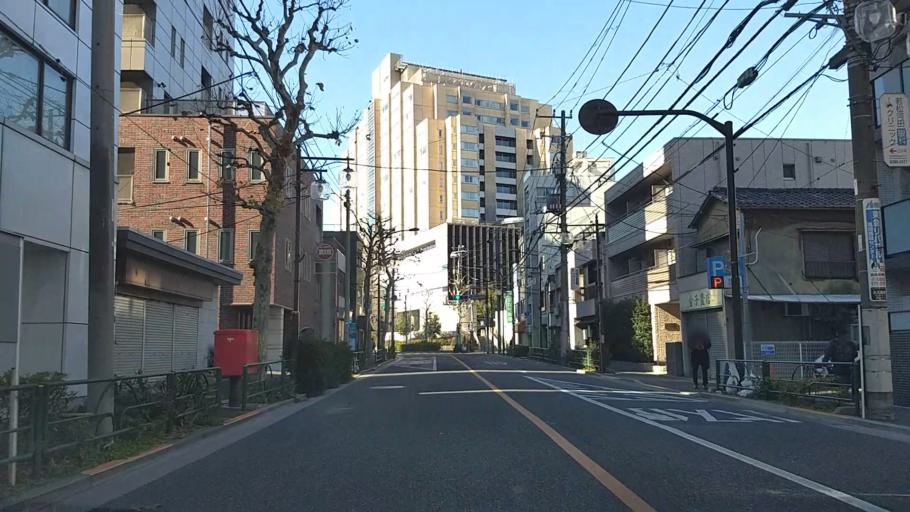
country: JP
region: Tokyo
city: Tokyo
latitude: 35.7011
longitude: 139.7185
